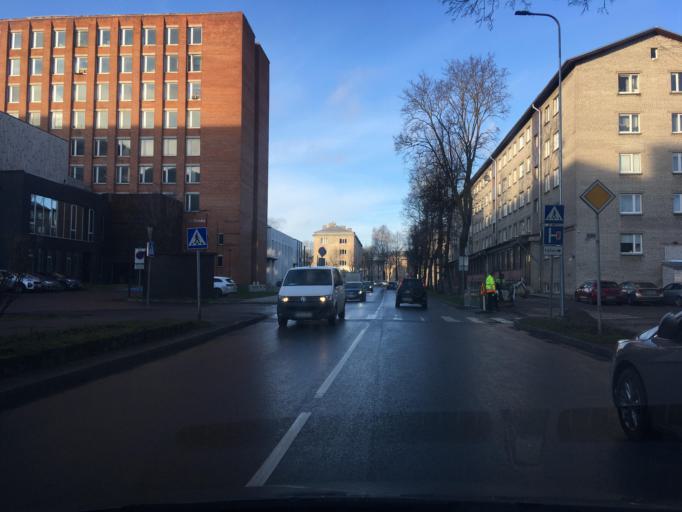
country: EE
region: Ida-Virumaa
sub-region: Narva linn
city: Narva
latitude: 59.3745
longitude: 28.1908
